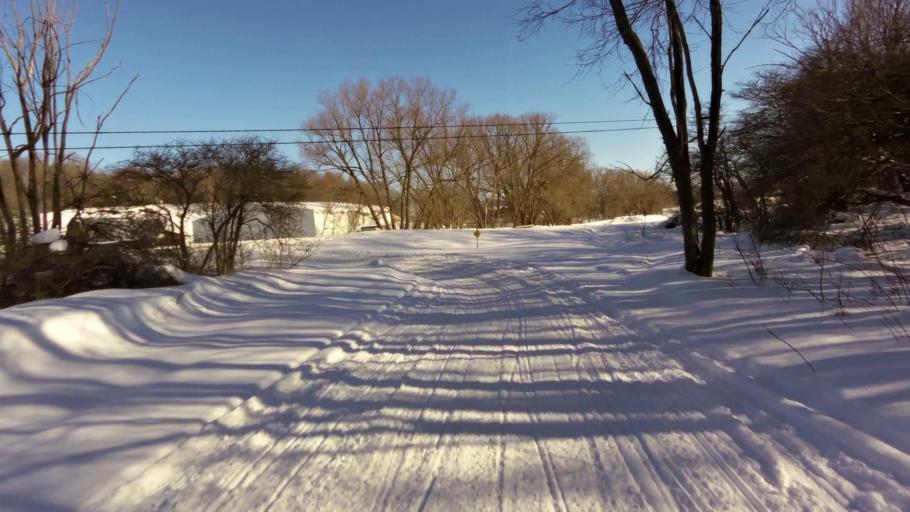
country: US
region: New York
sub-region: Cattaraugus County
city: Franklinville
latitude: 42.3917
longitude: -78.4860
